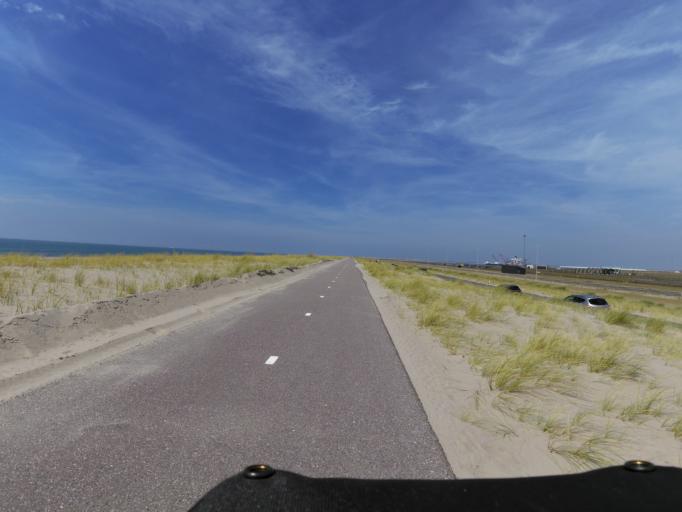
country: NL
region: South Holland
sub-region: Gemeente Goeree-Overflakkee
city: Goedereede
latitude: 51.9401
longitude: 3.9734
